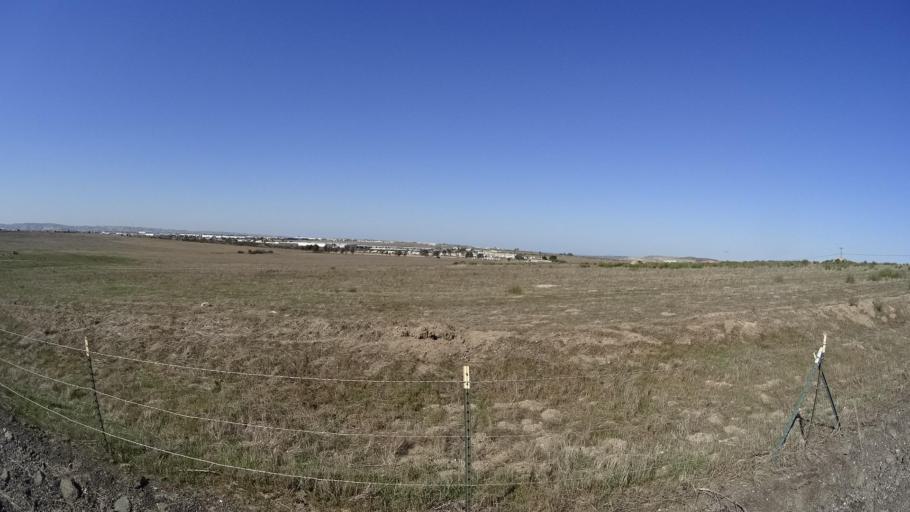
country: MX
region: Baja California
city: Tijuana
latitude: 32.5771
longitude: -116.9451
